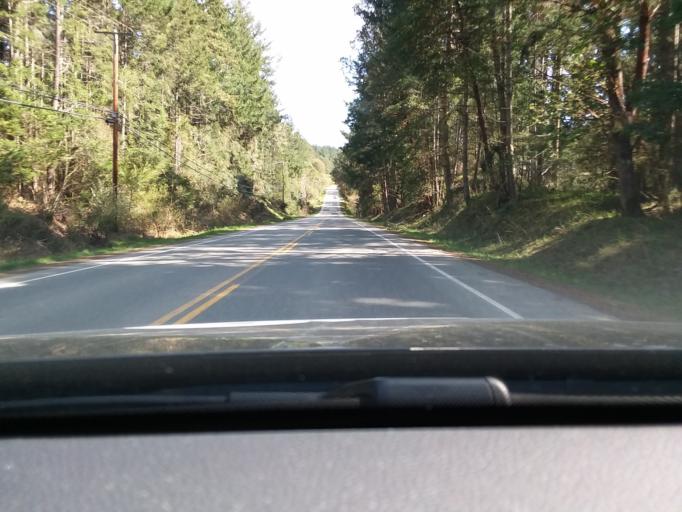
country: CA
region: British Columbia
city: North Saanich
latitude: 48.8573
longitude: -123.4806
